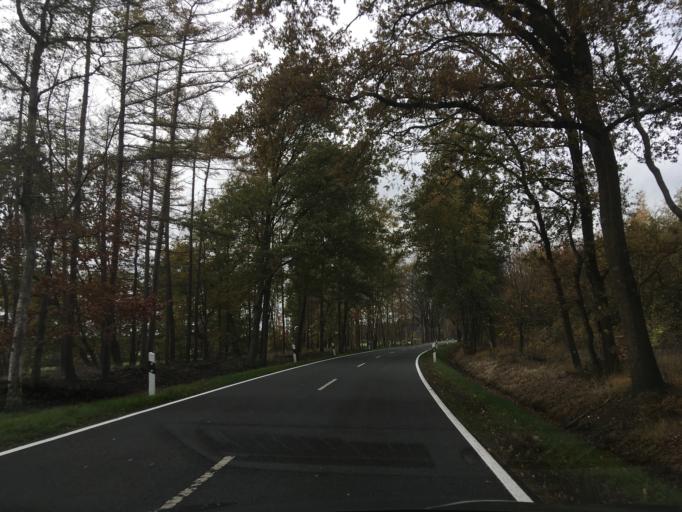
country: DE
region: North Rhine-Westphalia
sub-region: Regierungsbezirk Munster
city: Vreden
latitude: 52.0696
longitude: 6.8654
